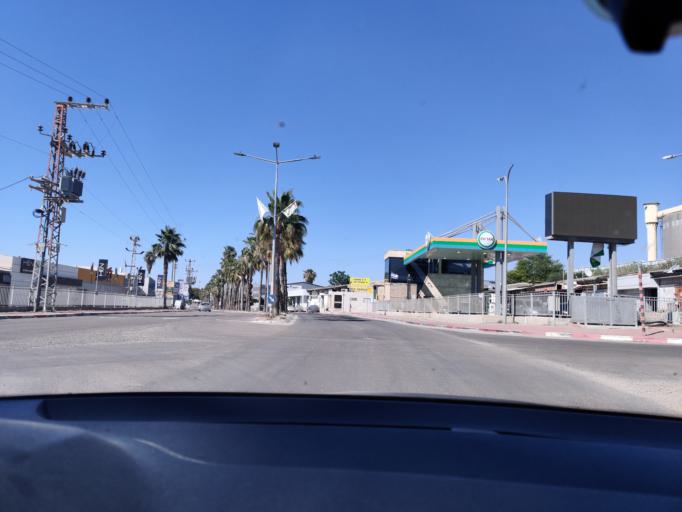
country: IL
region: Southern District
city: Qiryat Gat
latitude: 31.5993
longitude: 34.7786
